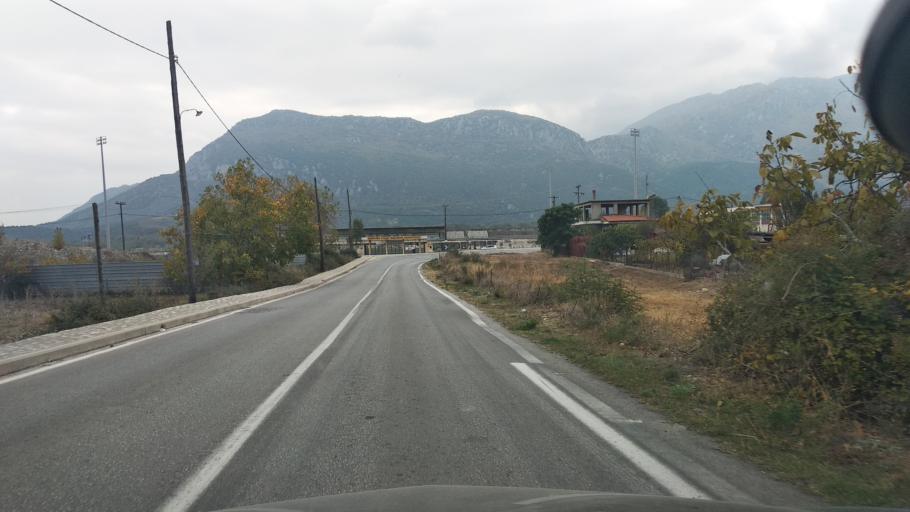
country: GR
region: Thessaly
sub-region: Trikala
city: Kalampaka
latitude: 39.7026
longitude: 21.6136
